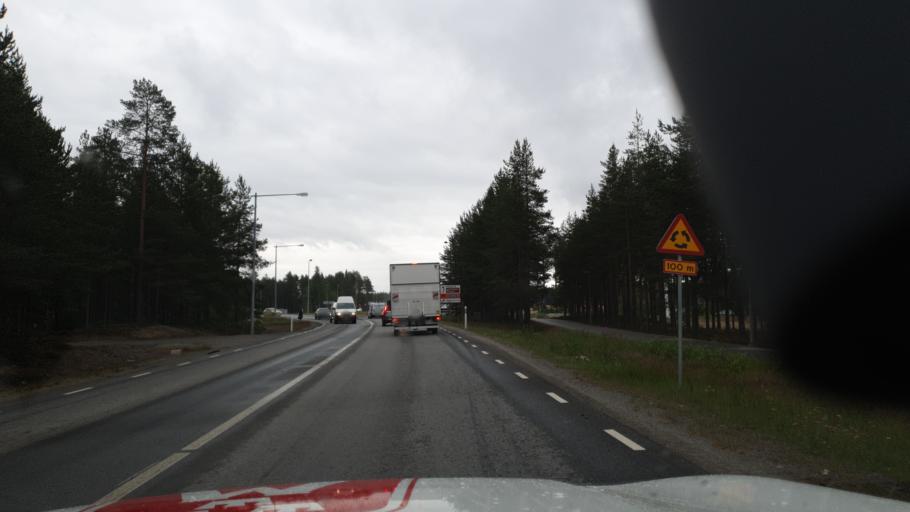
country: SE
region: Vaesterbotten
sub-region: Umea Kommun
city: Roback
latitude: 63.8482
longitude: 20.1576
